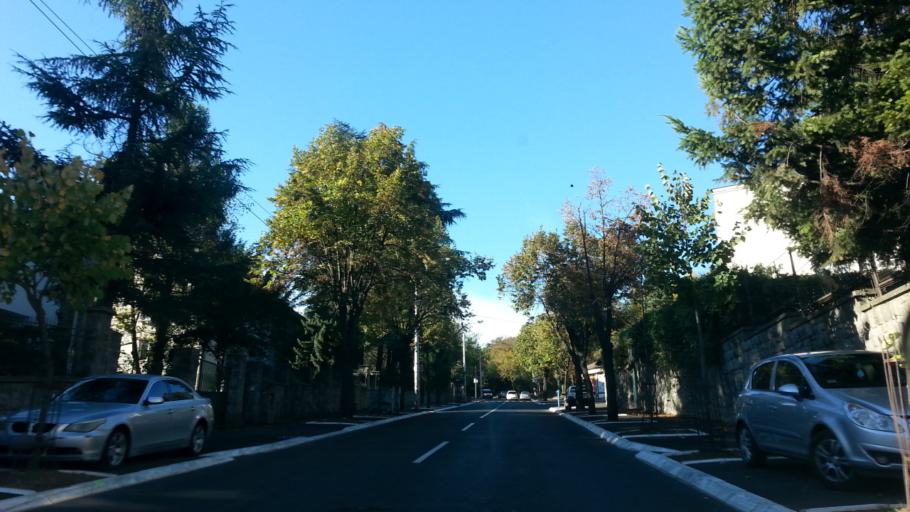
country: RS
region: Central Serbia
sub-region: Belgrade
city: Savski Venac
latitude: 44.7821
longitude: 20.4607
